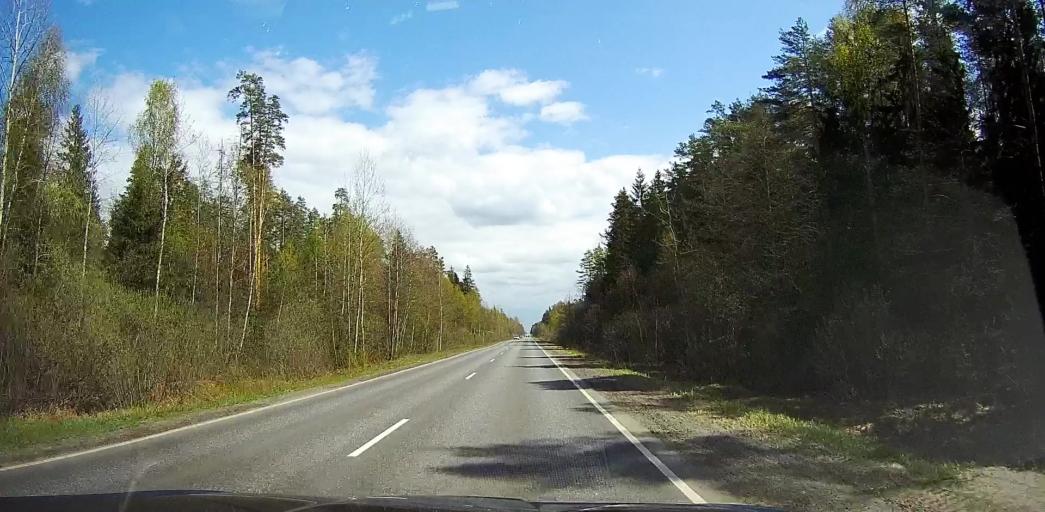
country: RU
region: Moskovskaya
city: Imeni Tsyurupy
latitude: 55.5514
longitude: 38.7317
